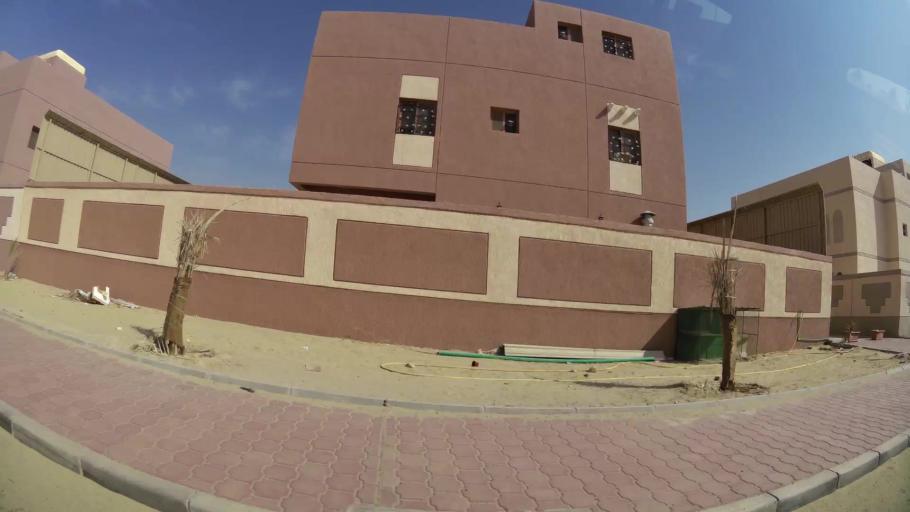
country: KW
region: Al Ahmadi
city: Al Wafrah
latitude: 28.8005
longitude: 48.0695
